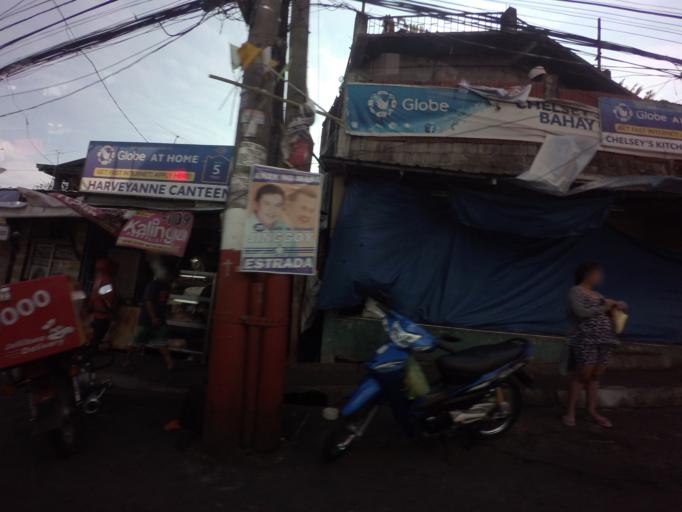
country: PH
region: Calabarzon
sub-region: Province of Rizal
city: Taguig
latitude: 14.5010
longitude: 121.0497
